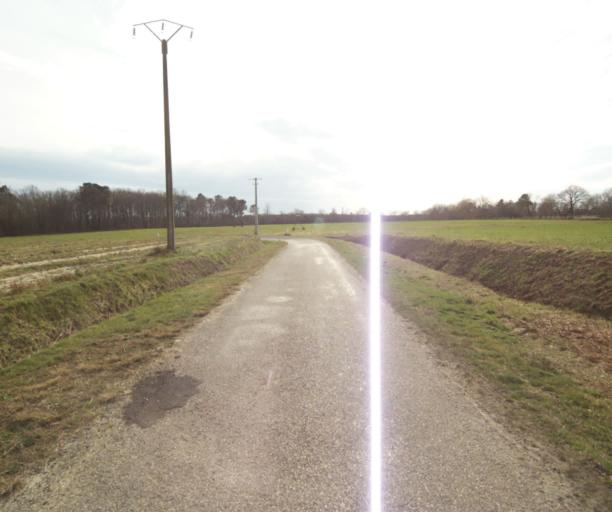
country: FR
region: Aquitaine
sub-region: Departement des Landes
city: Gabarret
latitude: 43.9893
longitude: 0.0402
